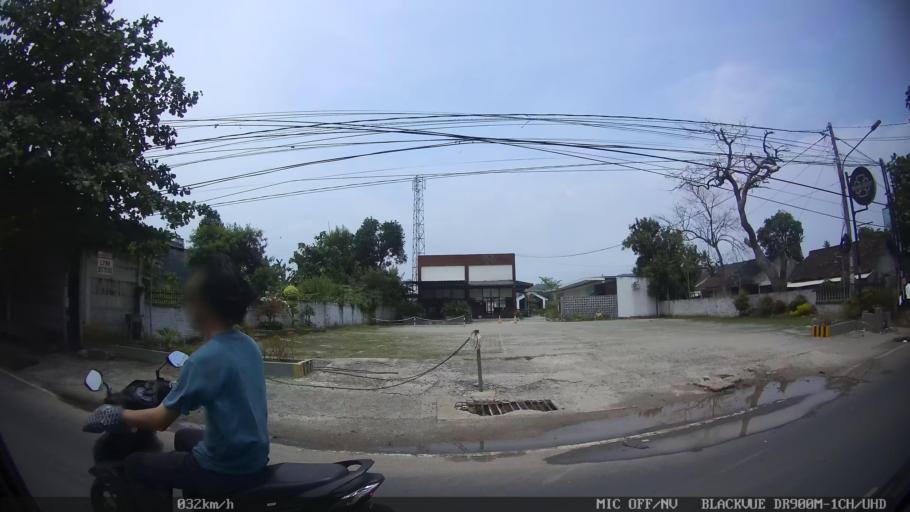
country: ID
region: Lampung
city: Bandarlampung
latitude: -5.4056
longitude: 105.2855
